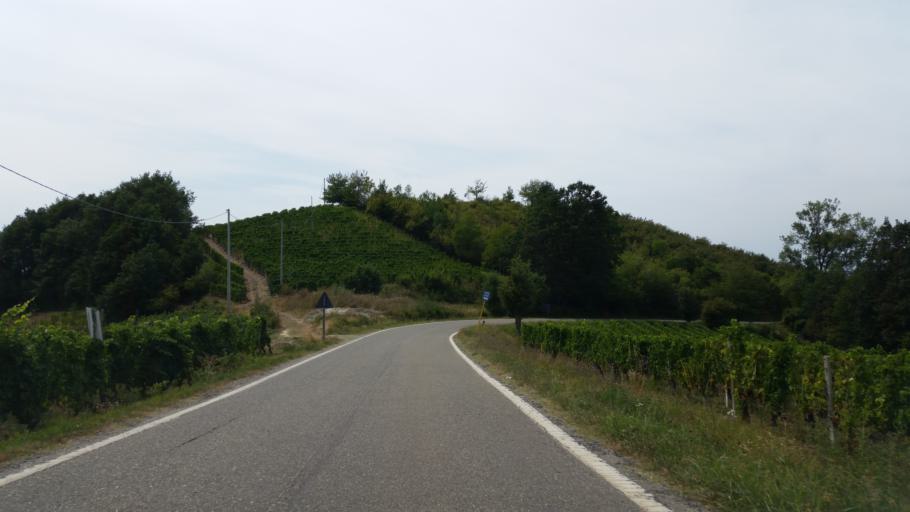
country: IT
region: Piedmont
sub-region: Provincia di Cuneo
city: Trezzo Tinella
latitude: 44.6577
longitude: 8.0972
